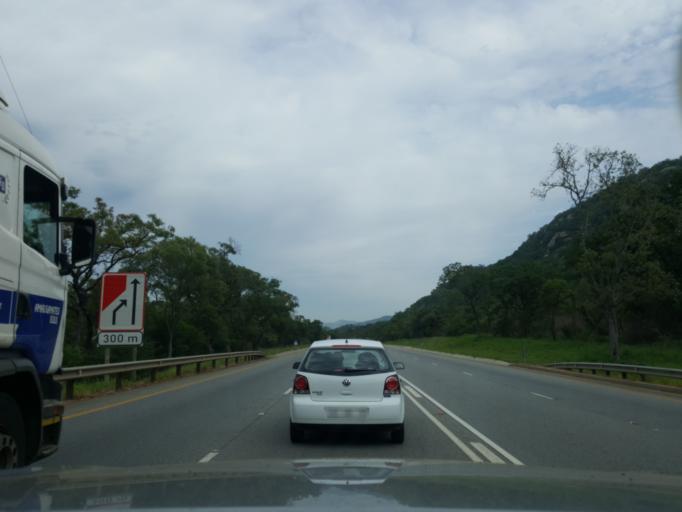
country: ZA
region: Mpumalanga
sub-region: Ehlanzeni District
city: Nelspruit
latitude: -25.5049
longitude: 31.1916
